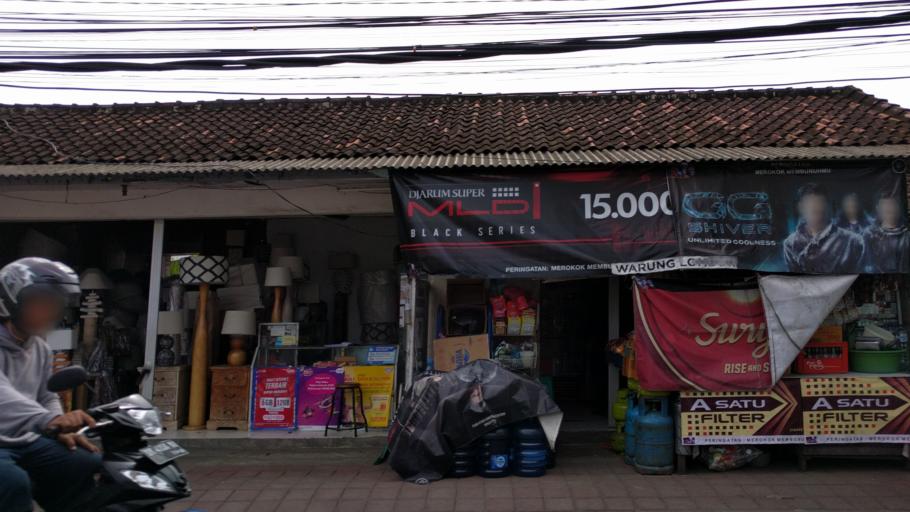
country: ID
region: Bali
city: Kuta
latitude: -8.6746
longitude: 115.1672
